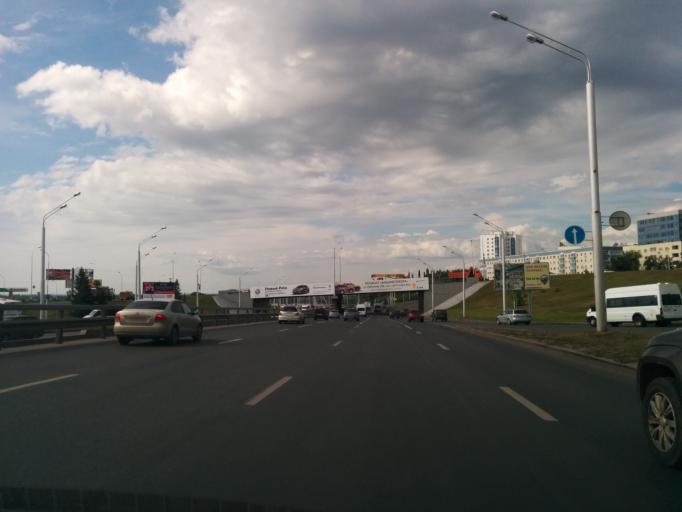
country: RU
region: Bashkortostan
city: Ufa
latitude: 54.7156
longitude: 55.9599
